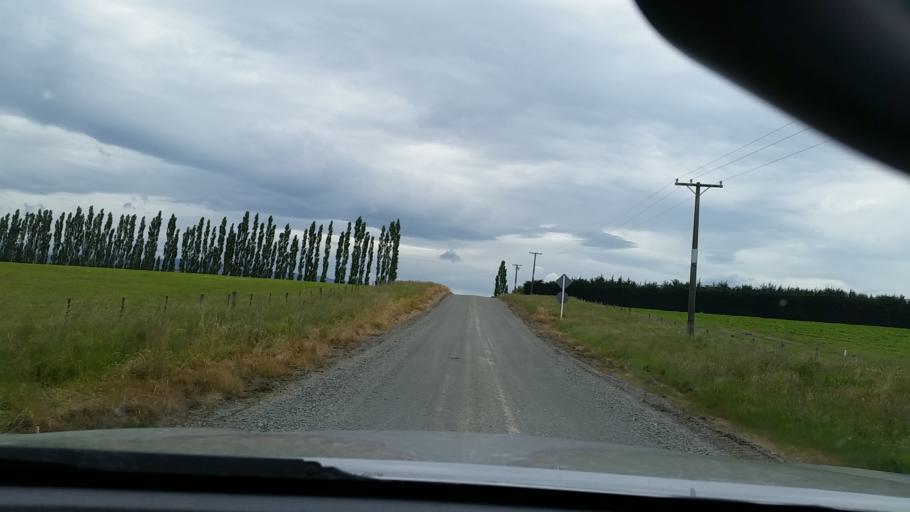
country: NZ
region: Southland
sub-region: Southland District
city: Winton
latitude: -45.8938
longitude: 168.1423
